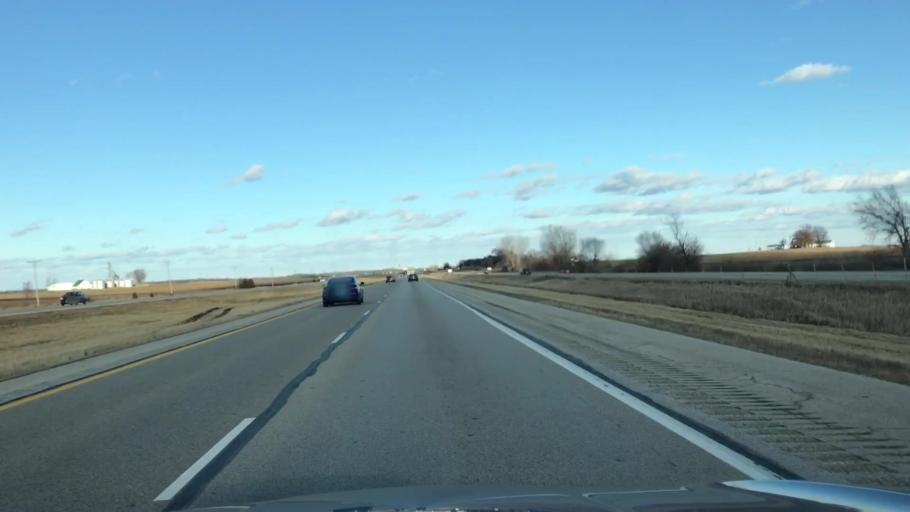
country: US
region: Illinois
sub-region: McLean County
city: Lexington
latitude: 40.6046
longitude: -88.8394
